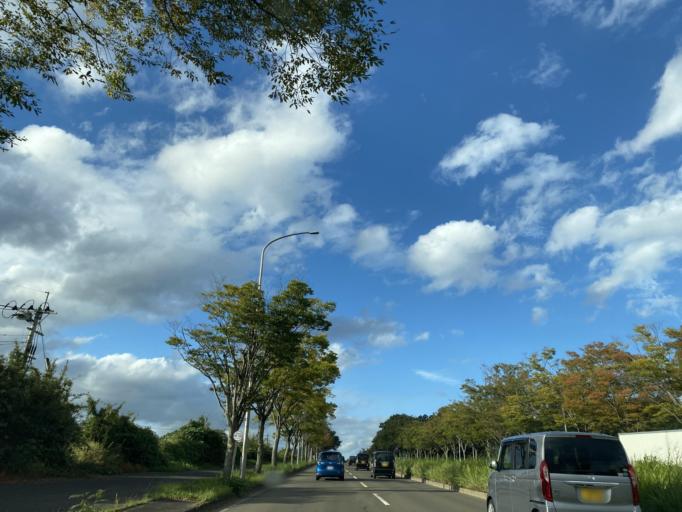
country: JP
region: Miyagi
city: Sendai-shi
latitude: 38.3307
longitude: 140.8407
